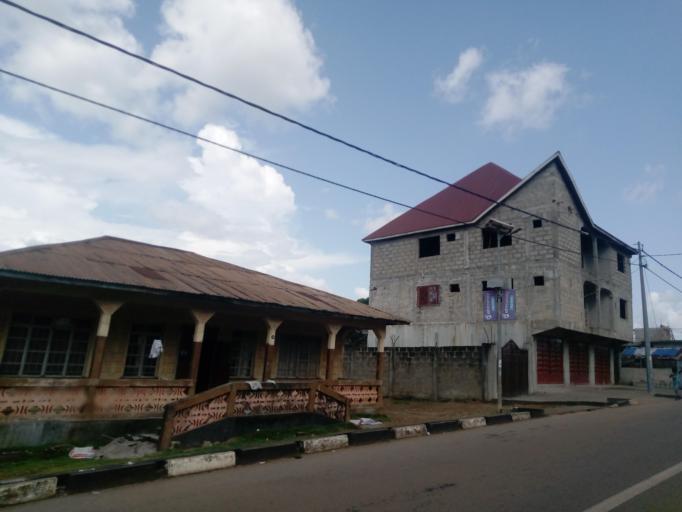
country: SL
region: Northern Province
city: Makeni
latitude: 8.8963
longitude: -12.0399
